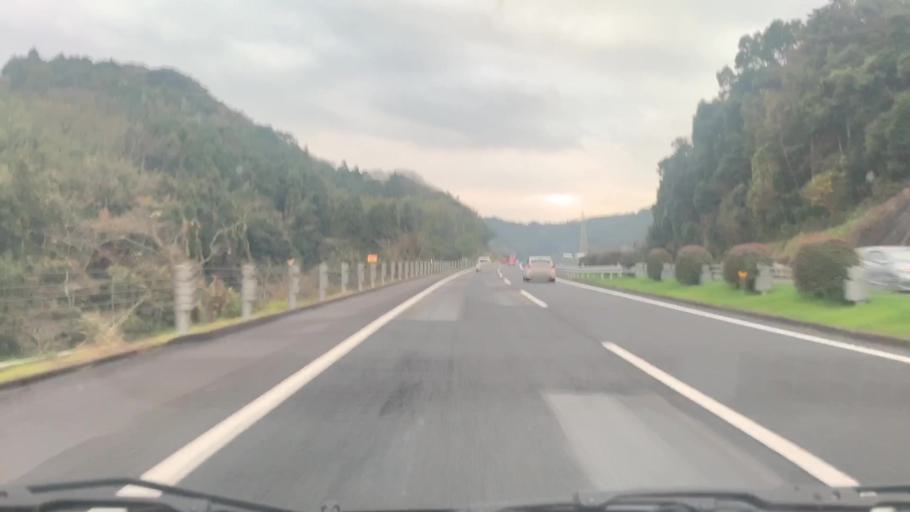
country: JP
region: Nagasaki
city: Omura
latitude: 32.8840
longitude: 129.9952
